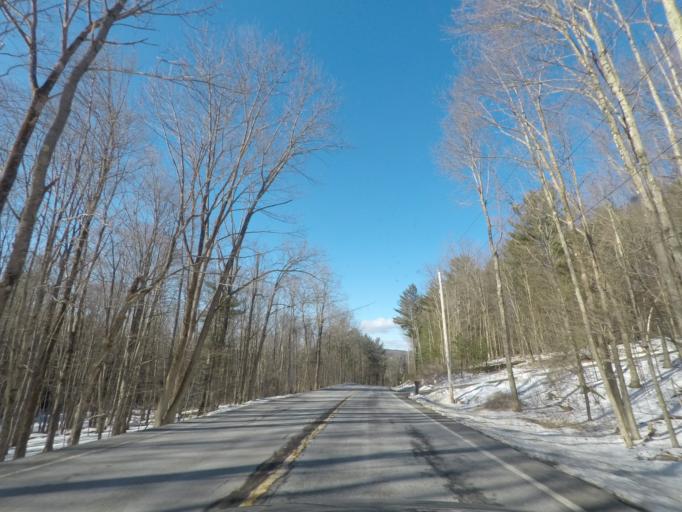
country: US
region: New York
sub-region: Columbia County
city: Chatham
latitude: 42.3515
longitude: -73.4824
